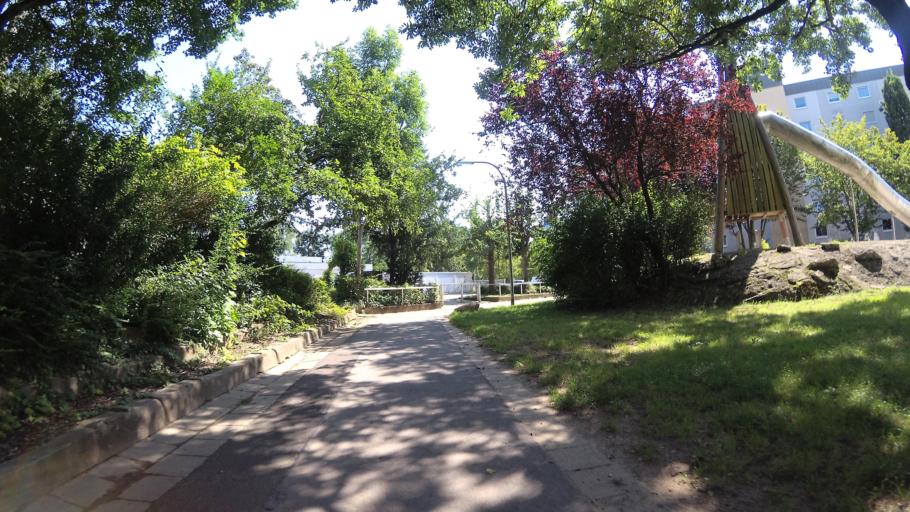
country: DE
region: Saarland
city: Saarbrucken
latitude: 49.2221
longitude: 6.9650
